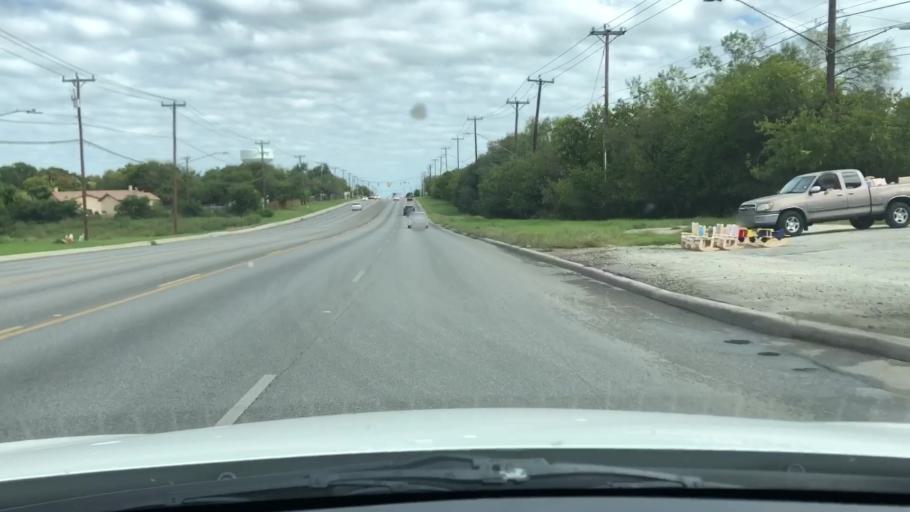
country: US
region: Texas
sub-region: Bexar County
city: Leon Valley
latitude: 29.4771
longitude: -98.6489
